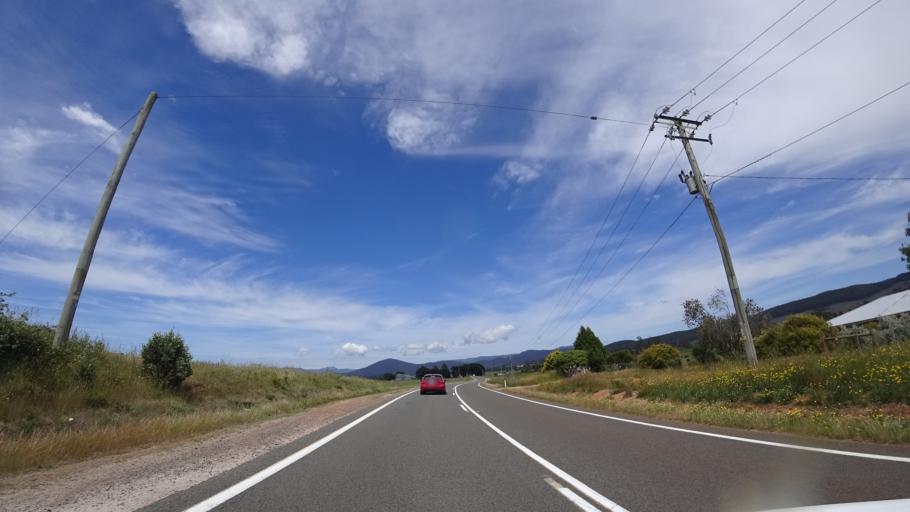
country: AU
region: Tasmania
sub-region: Dorset
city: Scottsdale
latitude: -41.1863
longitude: 147.7081
